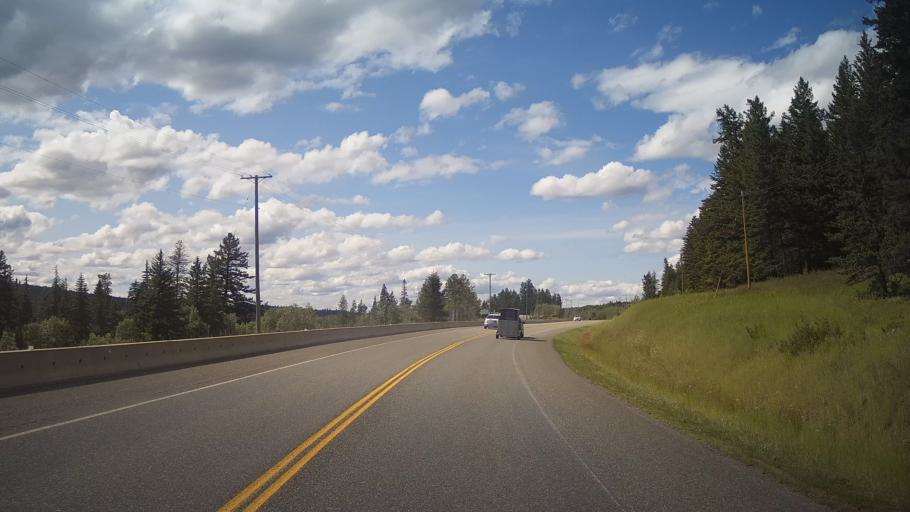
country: CA
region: British Columbia
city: Williams Lake
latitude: 51.8572
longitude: -121.6375
